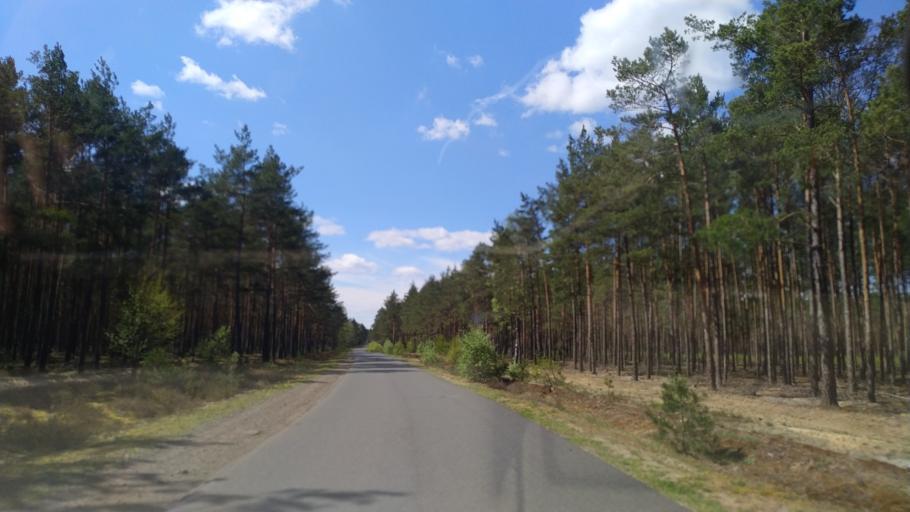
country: PL
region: Greater Poland Voivodeship
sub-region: Powiat zlotowski
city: Tarnowka
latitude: 53.2734
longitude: 16.8347
